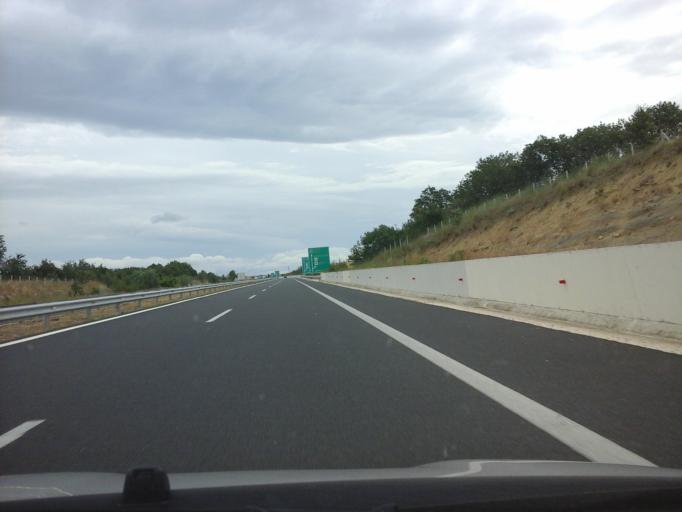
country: GR
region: East Macedonia and Thrace
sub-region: Nomos Evrou
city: Alexandroupoli
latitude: 40.9023
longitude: 25.9311
